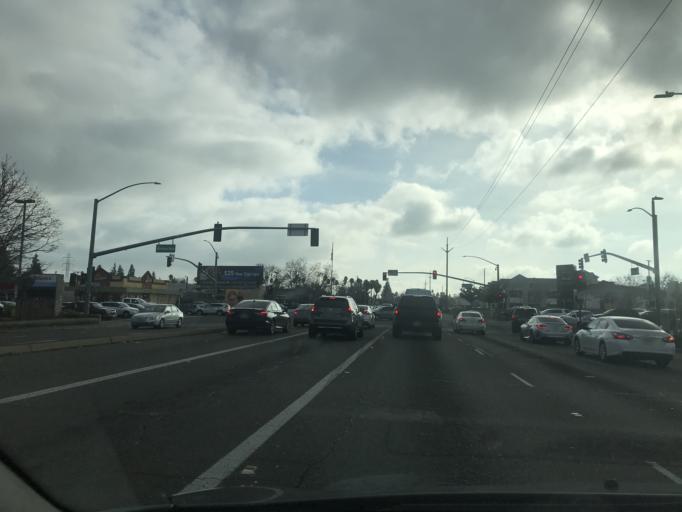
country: US
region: California
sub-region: Sacramento County
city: Arden-Arcade
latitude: 38.5968
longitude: -121.4154
